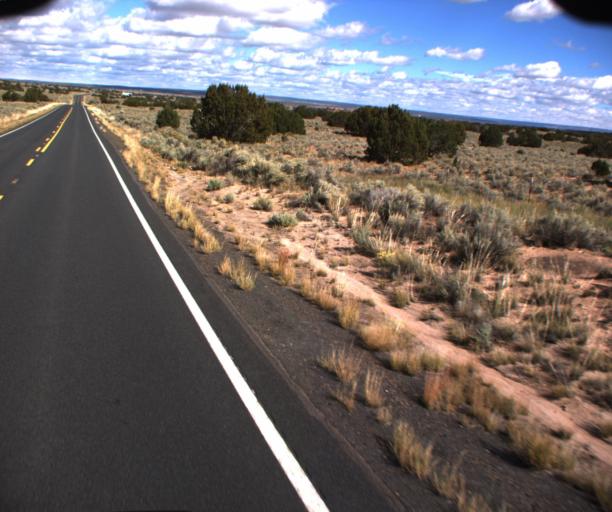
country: US
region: Arizona
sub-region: Apache County
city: Houck
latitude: 35.1586
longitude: -109.3362
